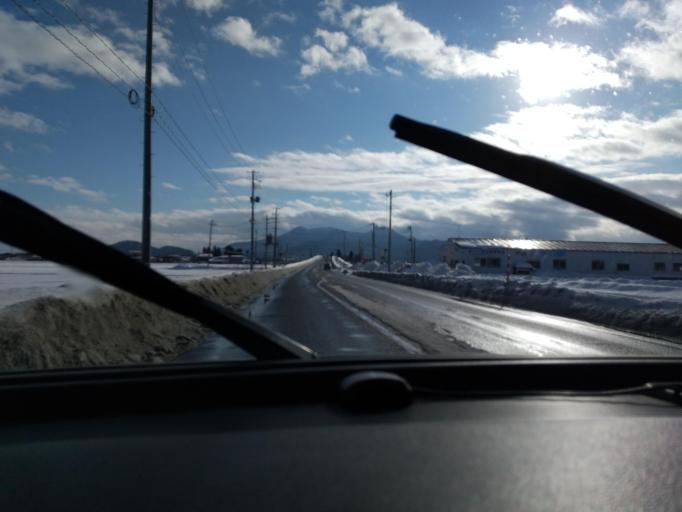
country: JP
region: Iwate
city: Morioka-shi
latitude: 39.7185
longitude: 141.0844
